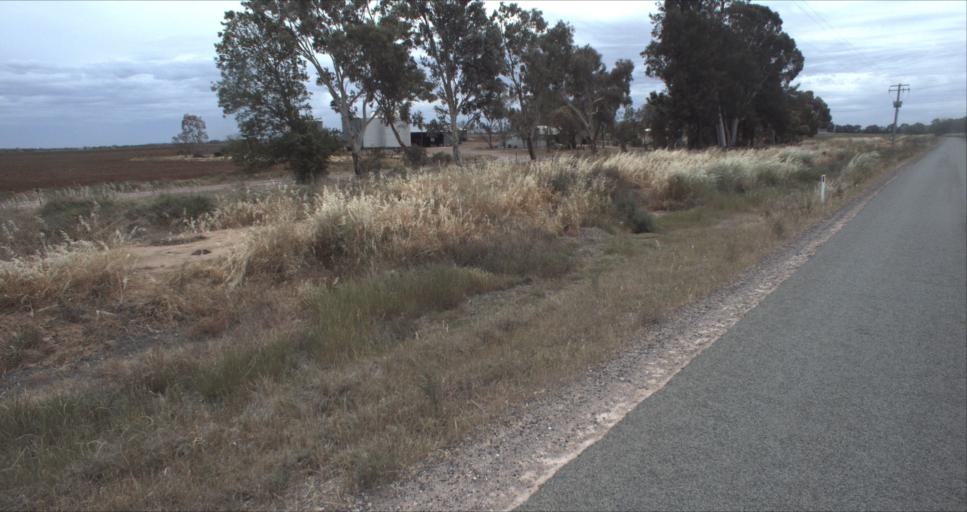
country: AU
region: New South Wales
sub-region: Leeton
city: Leeton
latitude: -34.4331
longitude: 146.3768
